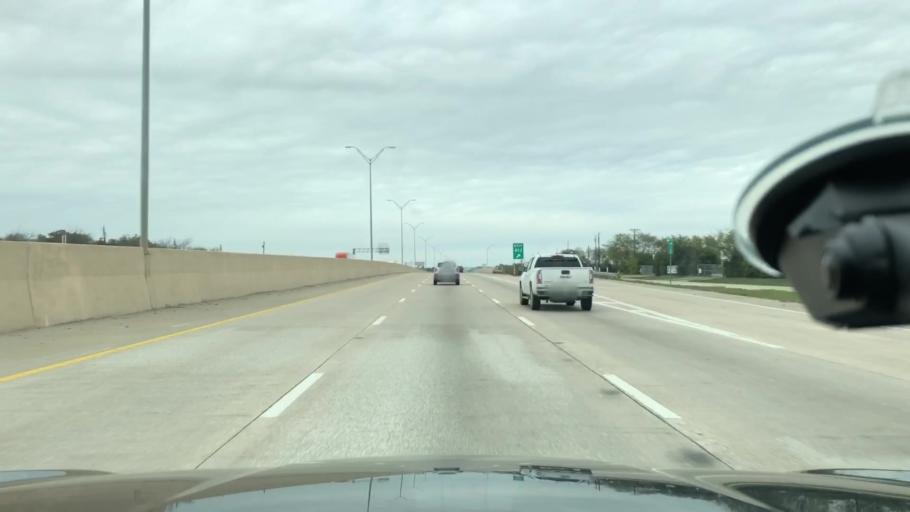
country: US
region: Texas
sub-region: Dallas County
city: Glenn Heights
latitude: 32.5476
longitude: -96.8223
